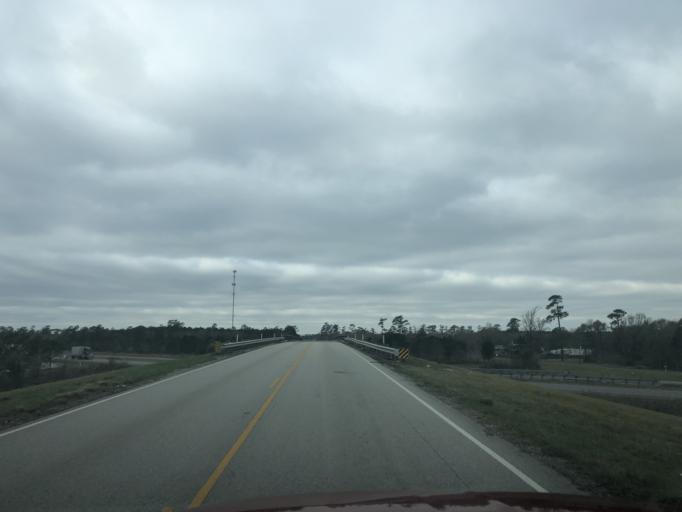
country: US
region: Texas
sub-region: Jefferson County
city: Fannett
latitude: 29.9316
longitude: -94.2673
